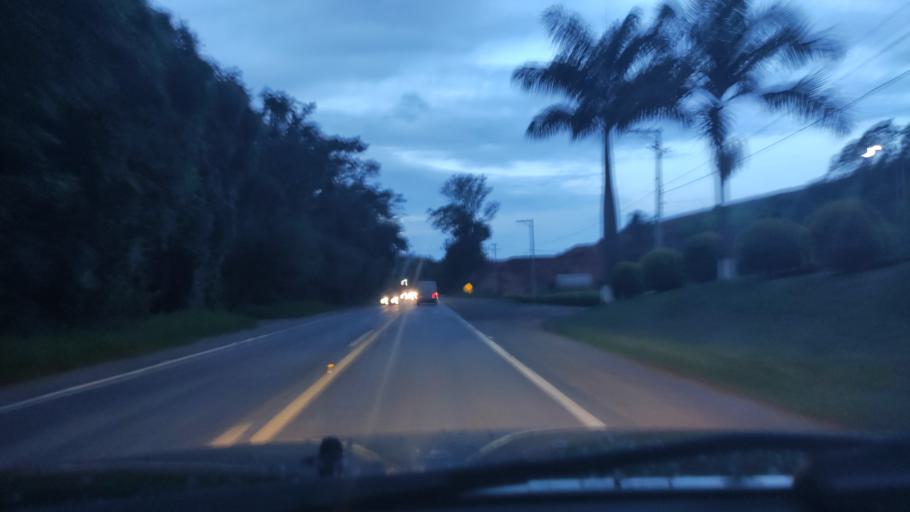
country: BR
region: Sao Paulo
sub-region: Socorro
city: Socorro
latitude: -22.6261
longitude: -46.5345
